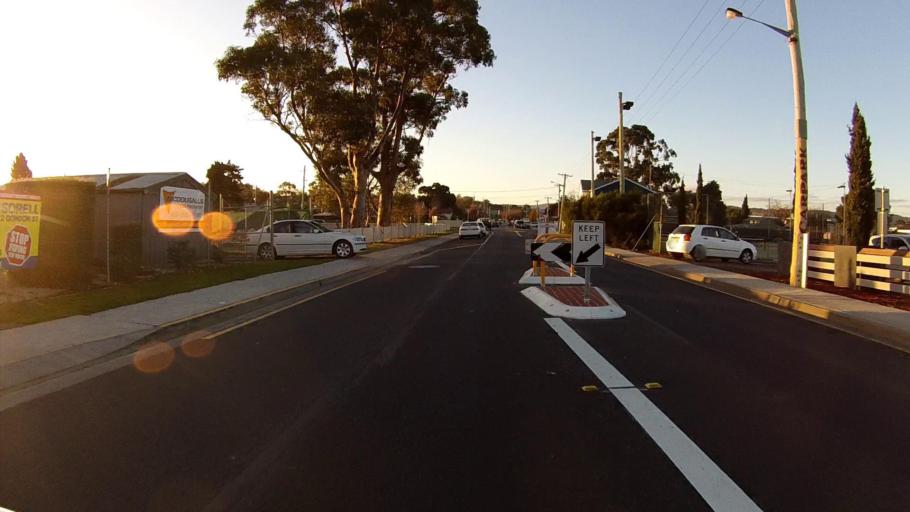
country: AU
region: Tasmania
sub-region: Sorell
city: Sorell
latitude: -42.7842
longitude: 147.5644
